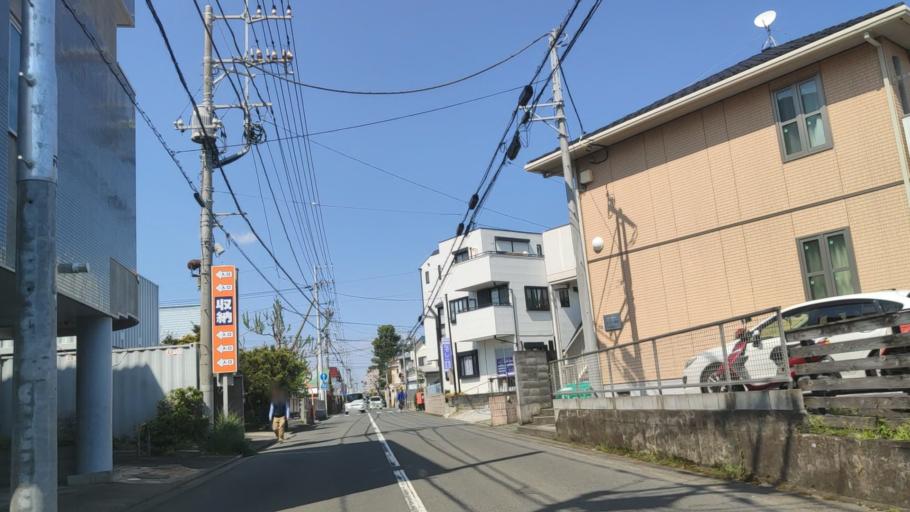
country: JP
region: Kanagawa
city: Hiratsuka
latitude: 35.3337
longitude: 139.3312
